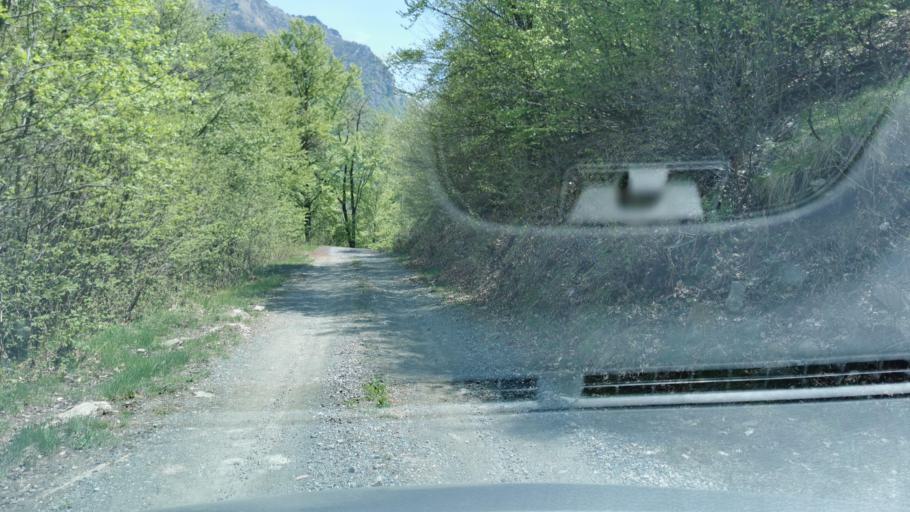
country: IT
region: Piedmont
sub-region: Provincia di Torino
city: Lemie
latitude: 45.2426
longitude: 7.2782
